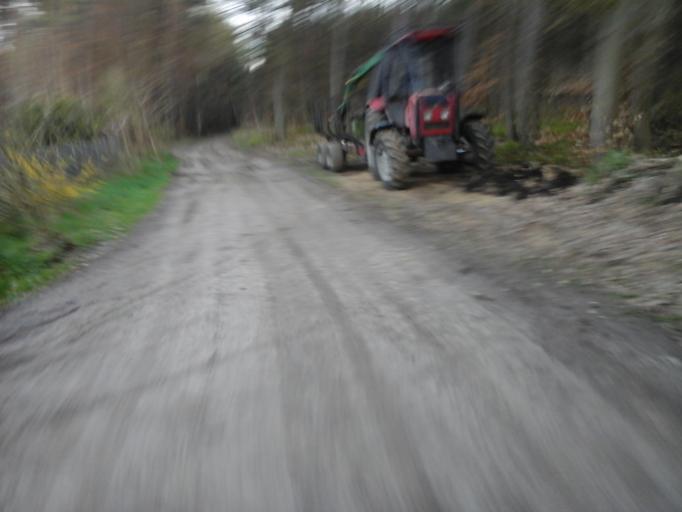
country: PL
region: West Pomeranian Voivodeship
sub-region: Powiat choszczenski
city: Bierzwnik
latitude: 53.0088
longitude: 15.6384
